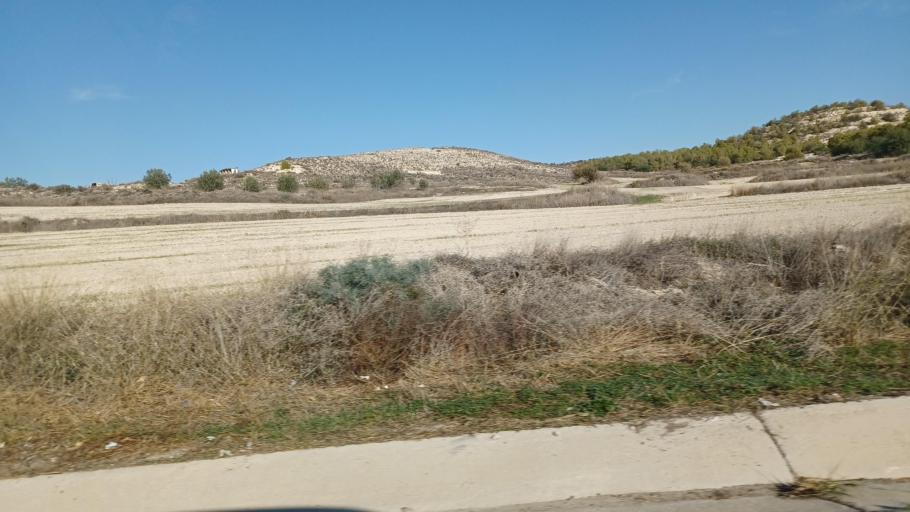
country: CY
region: Larnaka
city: Psevdas
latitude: 34.9704
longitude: 33.5262
